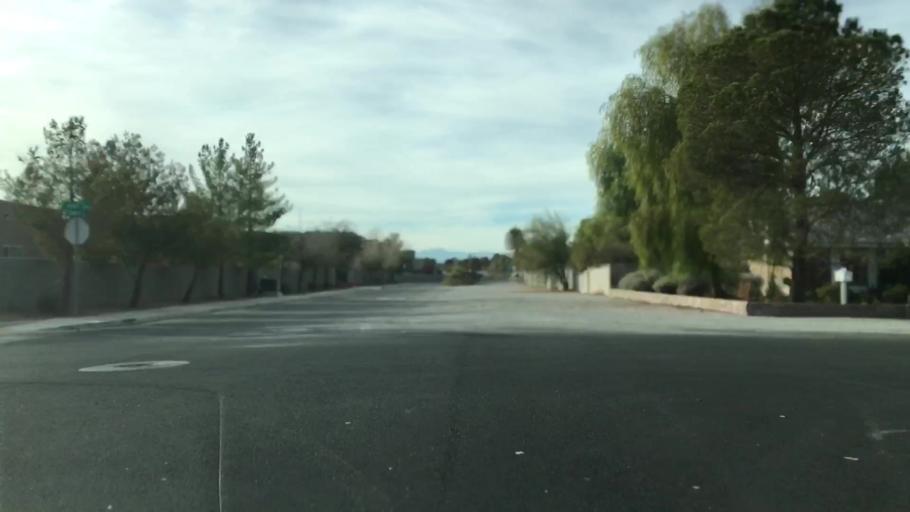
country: US
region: Nevada
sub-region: Clark County
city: Whitney
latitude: 36.0825
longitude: -115.0963
